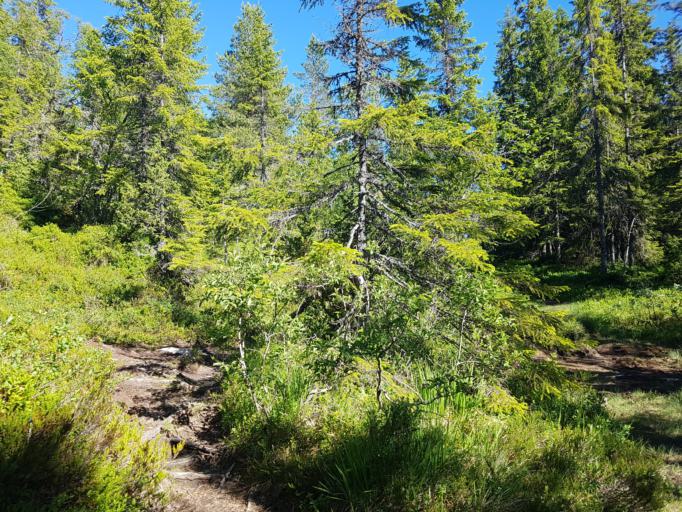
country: NO
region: Sor-Trondelag
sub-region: Trondheim
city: Trondheim
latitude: 63.4373
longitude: 10.2715
